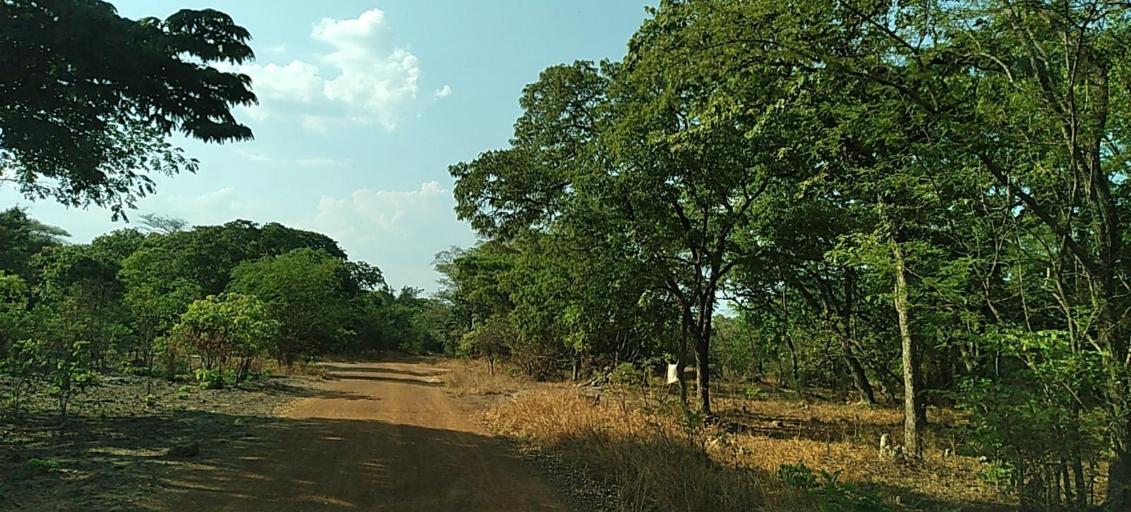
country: ZM
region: Copperbelt
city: Mpongwe
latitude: -13.4452
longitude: 28.0629
